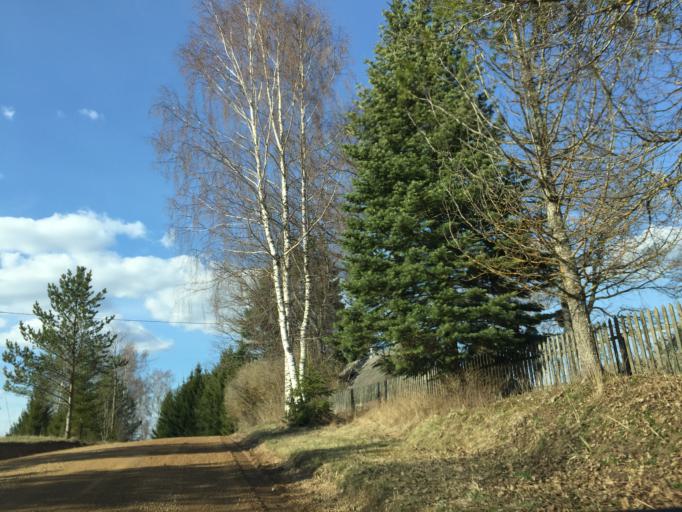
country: EE
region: Tartu
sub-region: Elva linn
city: Elva
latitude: 58.0906
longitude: 26.5133
